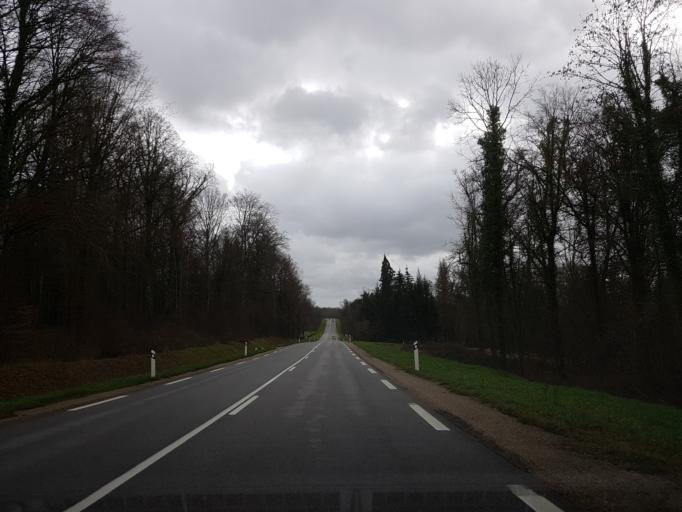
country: FR
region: Champagne-Ardenne
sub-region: Departement de la Haute-Marne
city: Fayl-Billot
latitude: 47.8024
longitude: 5.5596
